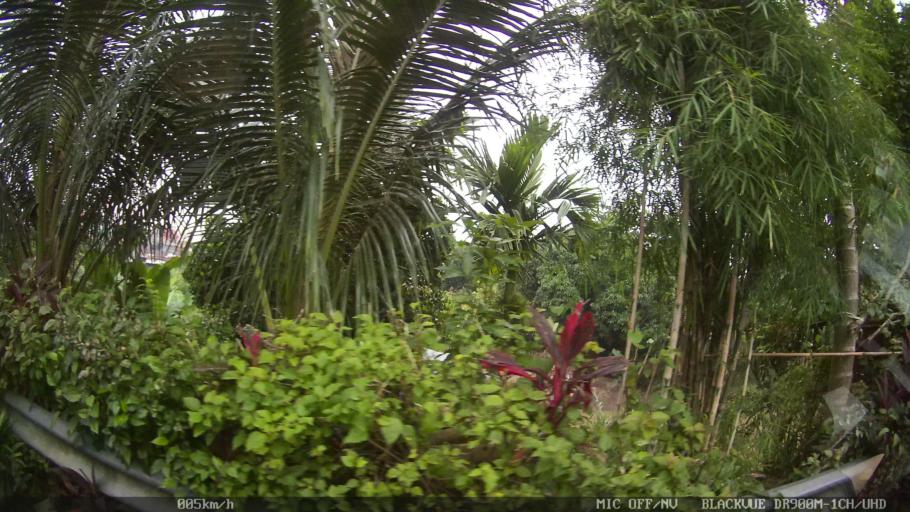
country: ID
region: North Sumatra
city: Deli Tua
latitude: 3.5512
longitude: 98.7135
